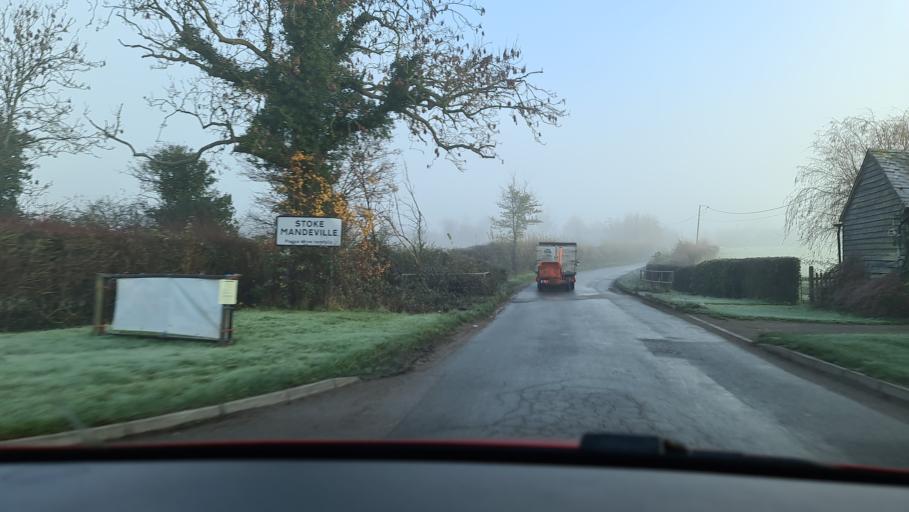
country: GB
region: England
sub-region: Buckinghamshire
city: Aylesbury
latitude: 51.7841
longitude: -0.7980
